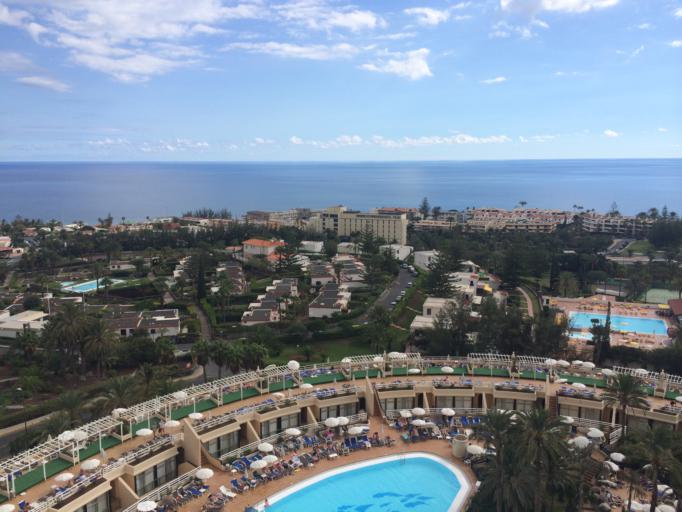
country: ES
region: Canary Islands
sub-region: Provincia de Las Palmas
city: Playa del Ingles
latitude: 27.7725
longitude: -15.5471
